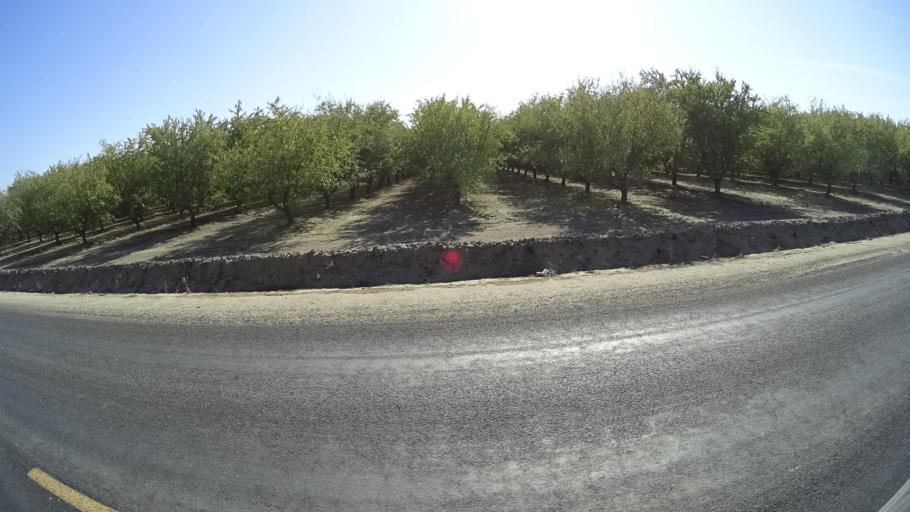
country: US
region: California
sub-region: Kern County
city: McFarland
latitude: 35.6453
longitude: -119.2868
